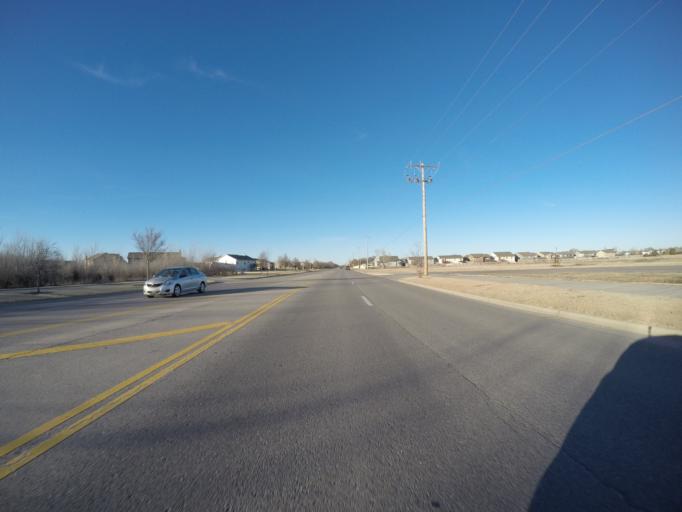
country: US
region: Kansas
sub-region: Sedgwick County
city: Goddard
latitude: 37.6512
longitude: -97.4808
